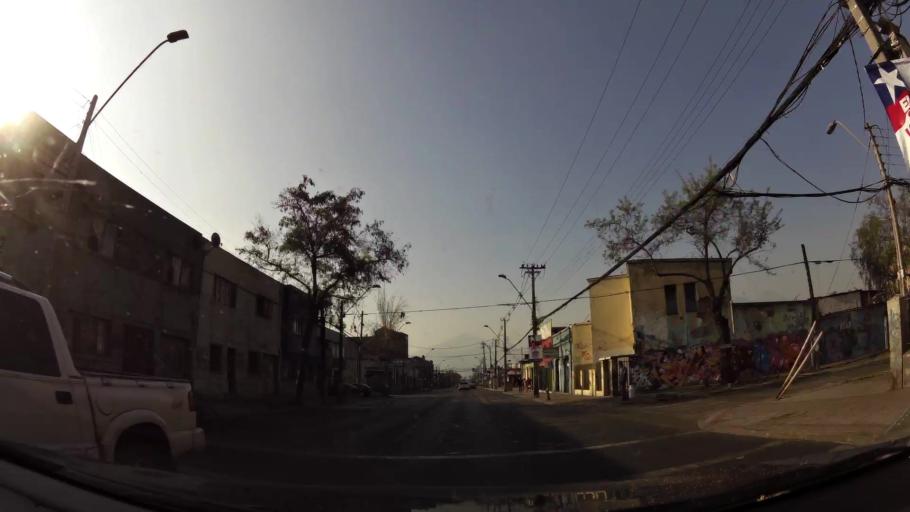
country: CL
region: Santiago Metropolitan
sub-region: Provincia de Santiago
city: Santiago
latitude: -33.4095
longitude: -70.6433
